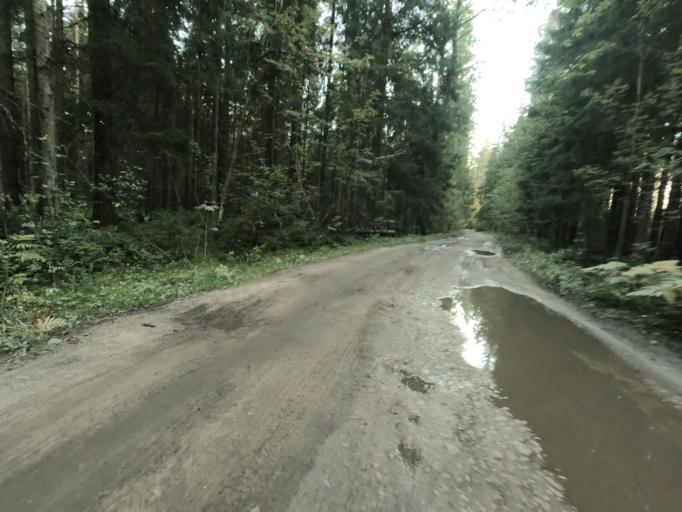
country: RU
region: Leningrad
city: Otradnoye
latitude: 59.8250
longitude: 30.7734
